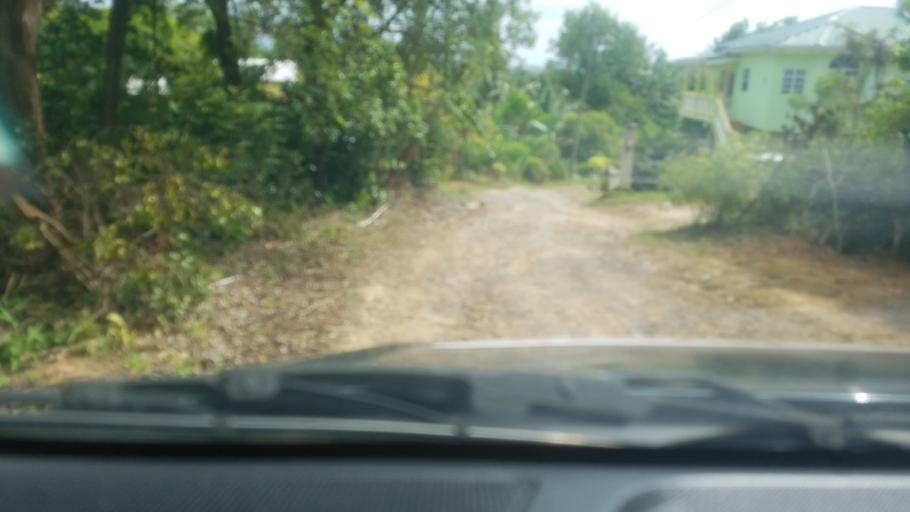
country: LC
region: Micoud Quarter
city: Micoud
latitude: 13.7945
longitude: -60.9261
